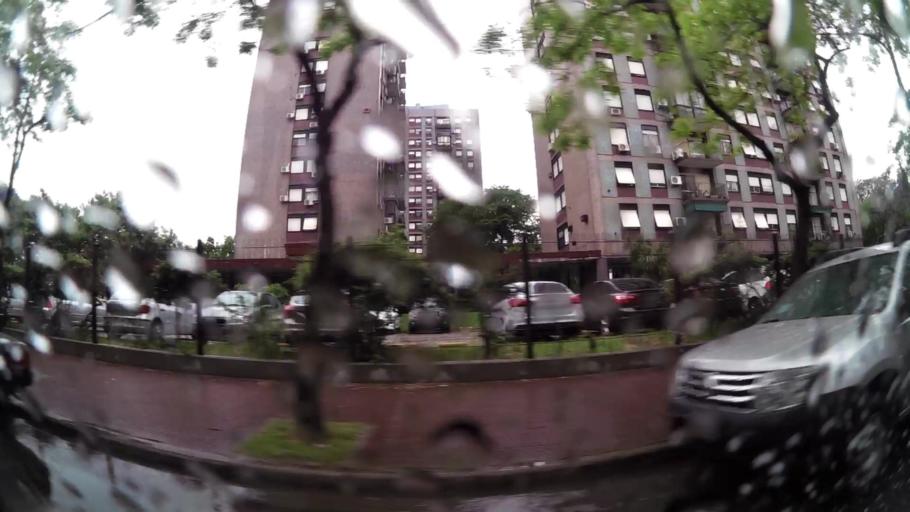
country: AR
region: Buenos Aires F.D.
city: Buenos Aires
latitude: -34.6268
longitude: -58.3618
